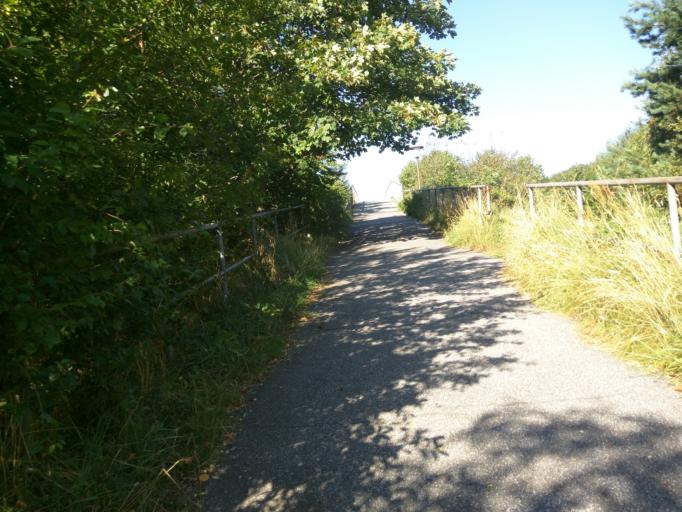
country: DK
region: Central Jutland
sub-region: Viborg Kommune
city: Viborg
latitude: 56.4379
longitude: 9.3876
